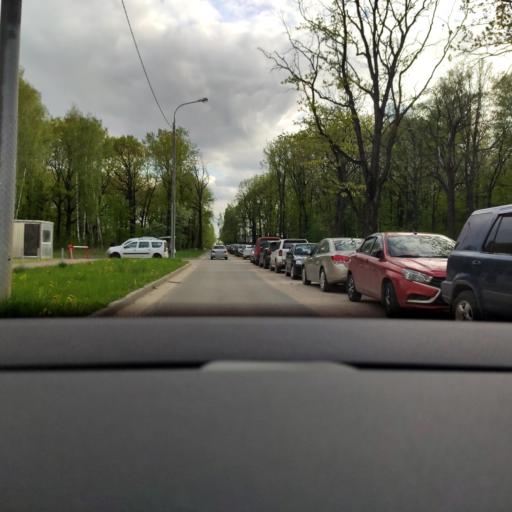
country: RU
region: Moskovskaya
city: Reutov
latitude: 55.7766
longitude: 37.8886
